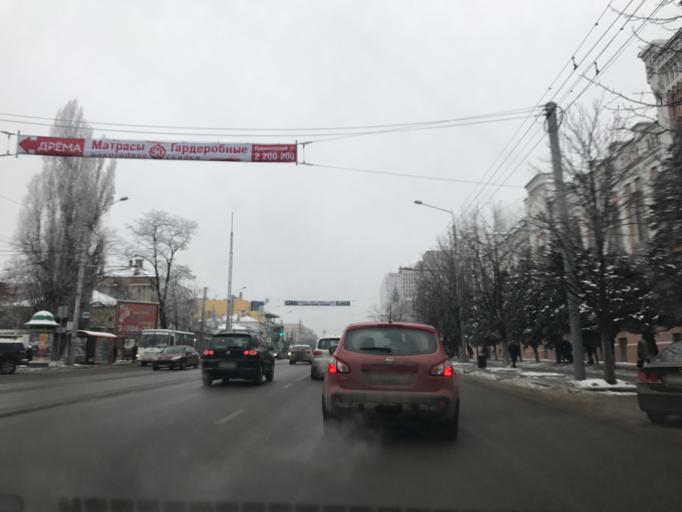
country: RU
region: Rostov
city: Rostov-na-Donu
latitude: 47.2299
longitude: 39.7033
